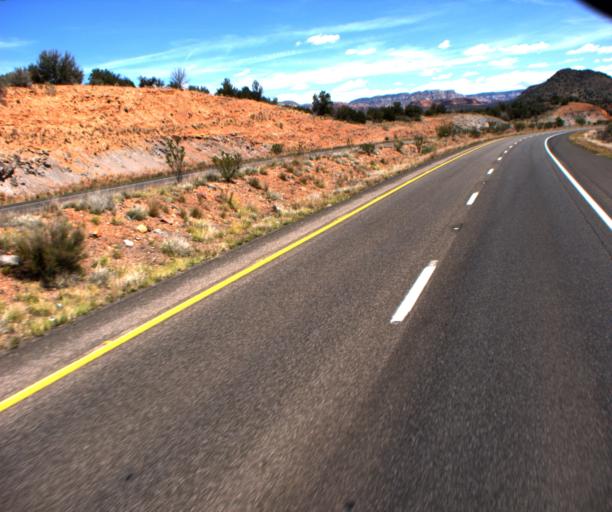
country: US
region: Arizona
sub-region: Yavapai County
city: West Sedona
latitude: 34.8350
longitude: -111.8899
